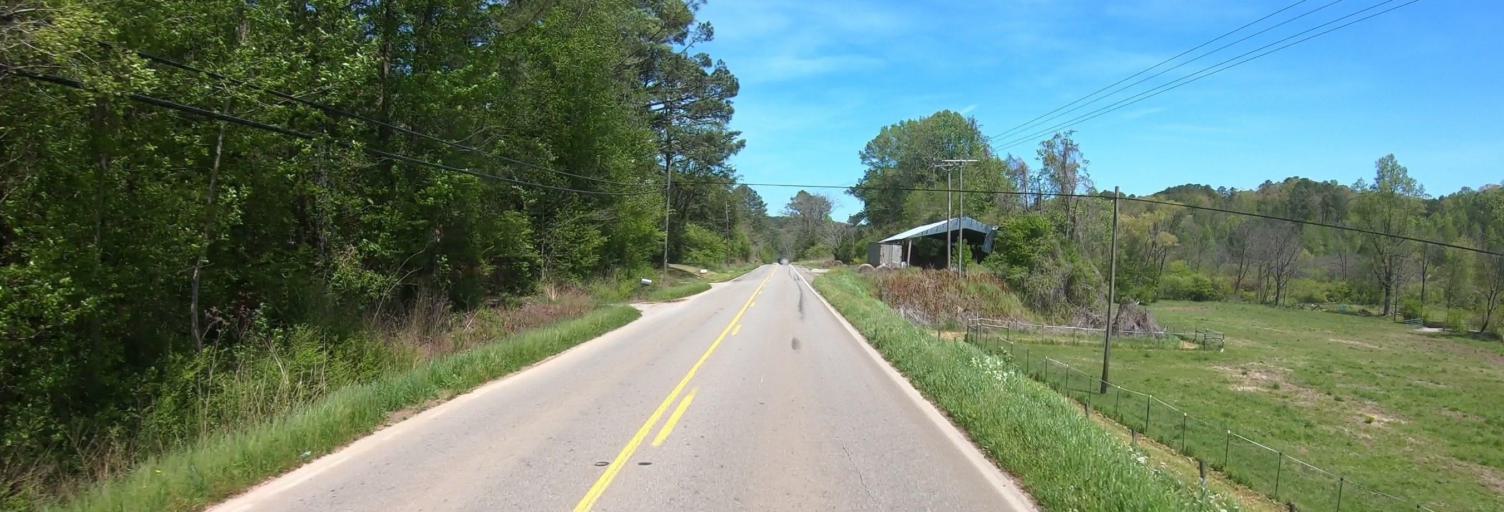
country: US
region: Georgia
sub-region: Gilmer County
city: Ellijay
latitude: 34.5727
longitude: -84.5356
